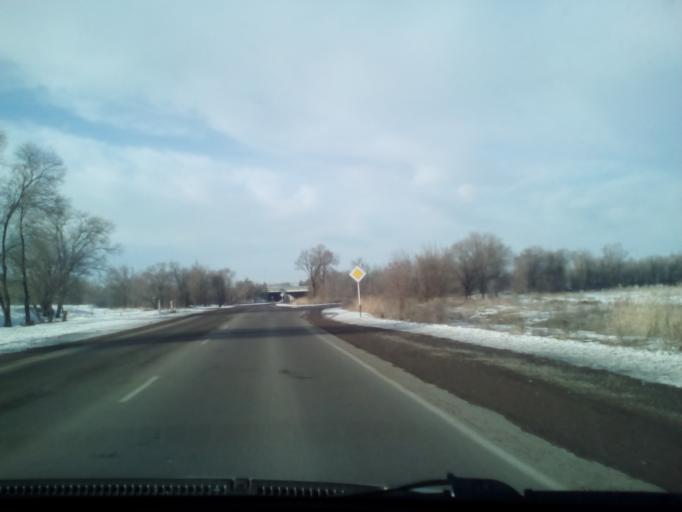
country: KZ
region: Almaty Oblysy
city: Burunday
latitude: 43.2195
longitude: 76.4106
